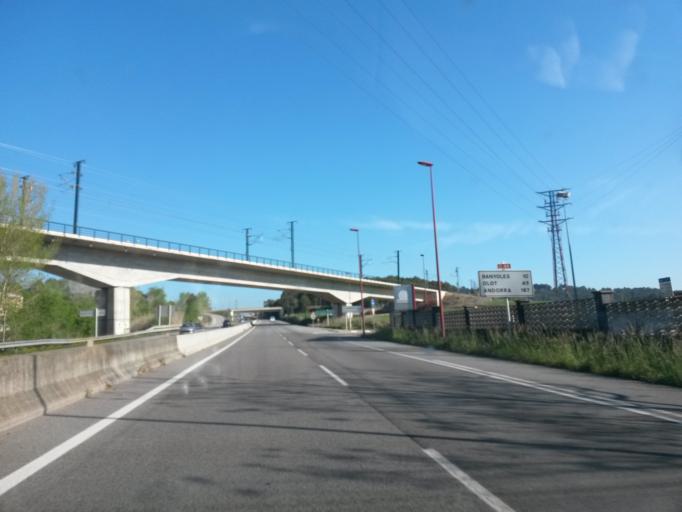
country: ES
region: Catalonia
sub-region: Provincia de Girona
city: Sarria de Ter
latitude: 42.0391
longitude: 2.8227
